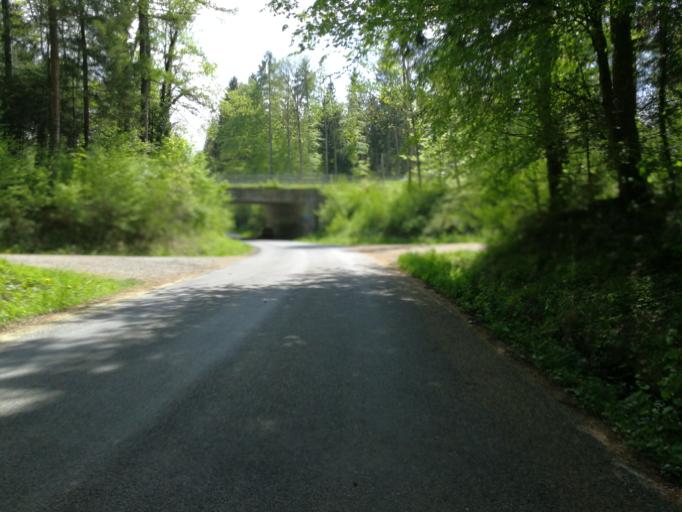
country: CH
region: Zurich
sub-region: Bezirk Hinwil
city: Binzikon
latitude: 47.2904
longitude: 8.7564
